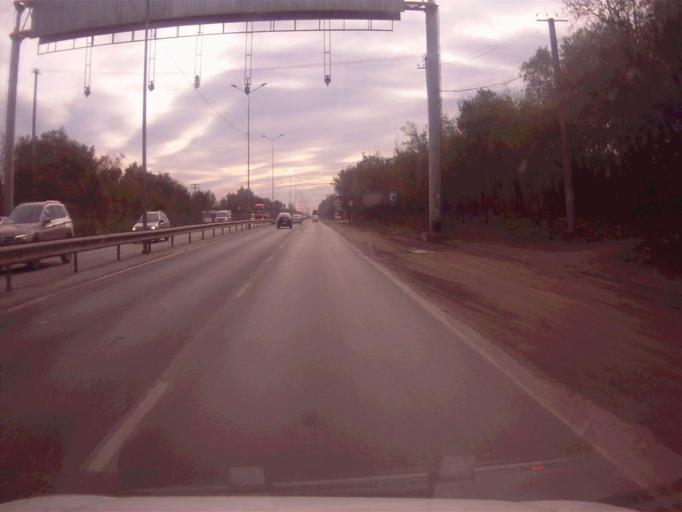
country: RU
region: Chelyabinsk
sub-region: Gorod Chelyabinsk
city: Chelyabinsk
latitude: 55.1084
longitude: 61.4085
